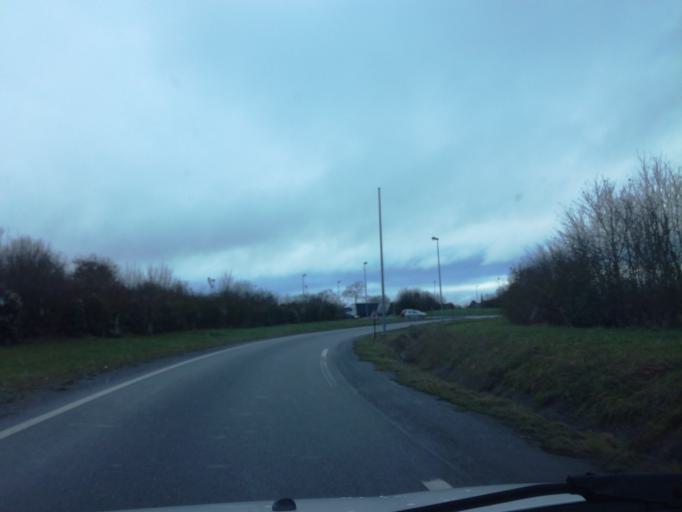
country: FR
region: Brittany
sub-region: Departement d'Ille-et-Vilaine
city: Chartres-de-Bretagne
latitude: 48.0491
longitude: -1.7098
